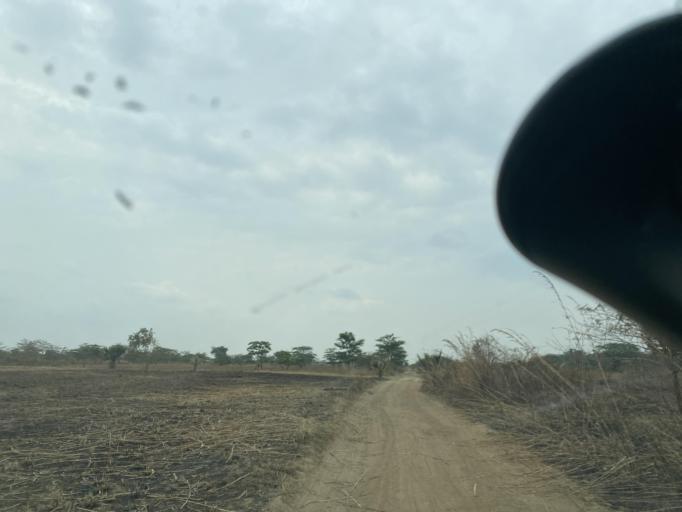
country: ZM
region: Lusaka
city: Lusaka
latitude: -15.2422
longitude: 28.3332
